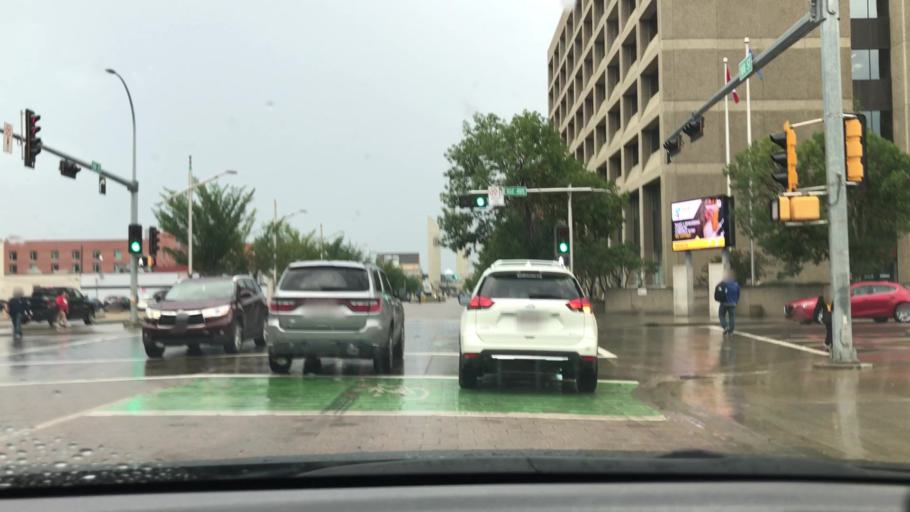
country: CA
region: Alberta
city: Edmonton
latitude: 53.5427
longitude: -113.5067
